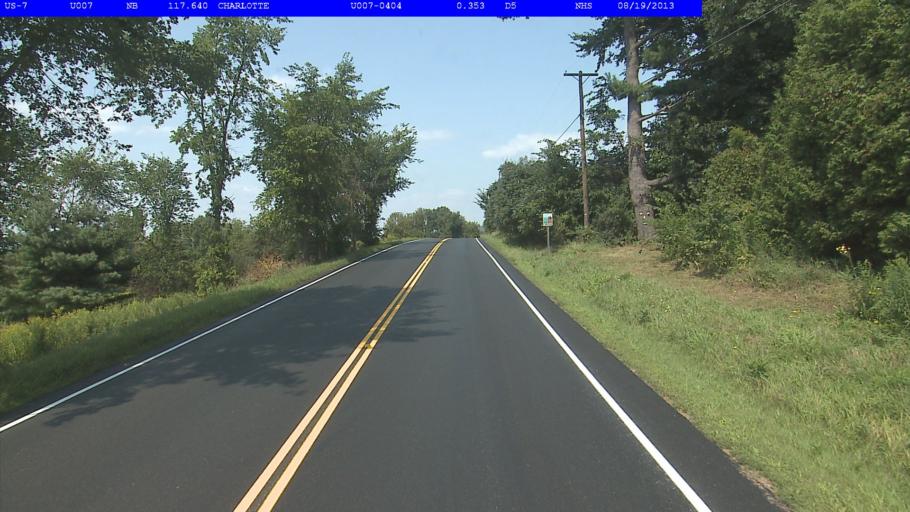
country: US
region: Vermont
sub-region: Addison County
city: Vergennes
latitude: 44.2673
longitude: -73.2328
